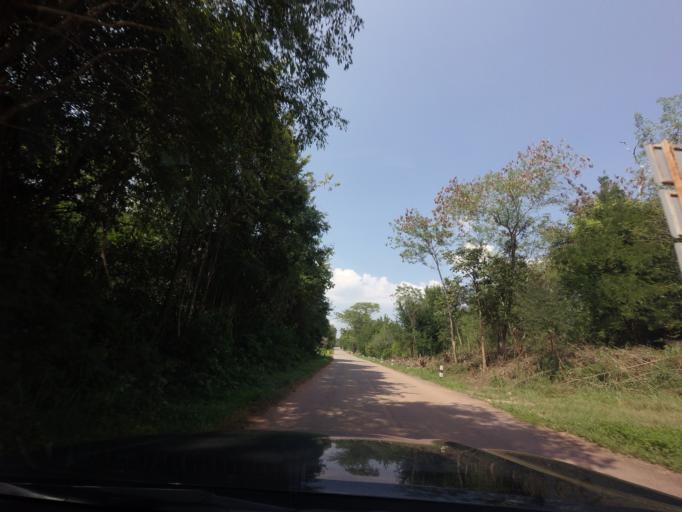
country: TH
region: Uttaradit
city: Fak Tha
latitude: 17.8800
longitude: 100.9763
